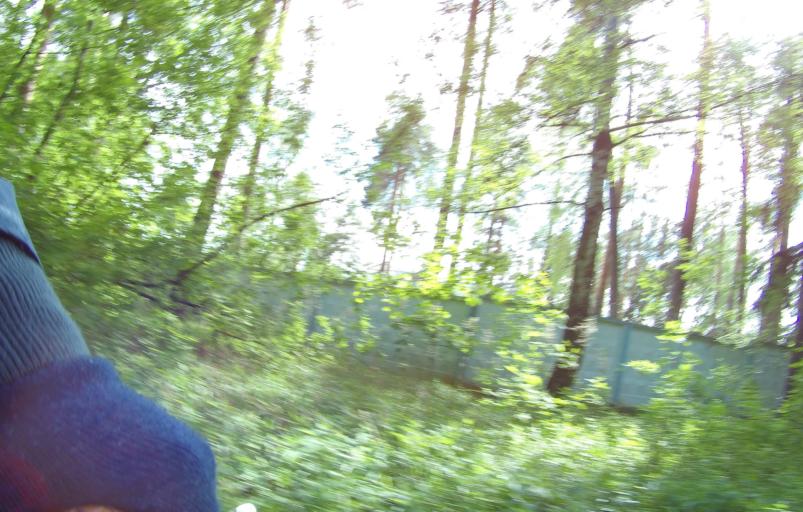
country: RU
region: Moskovskaya
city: Ramenskoye
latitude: 55.5713
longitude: 38.1997
